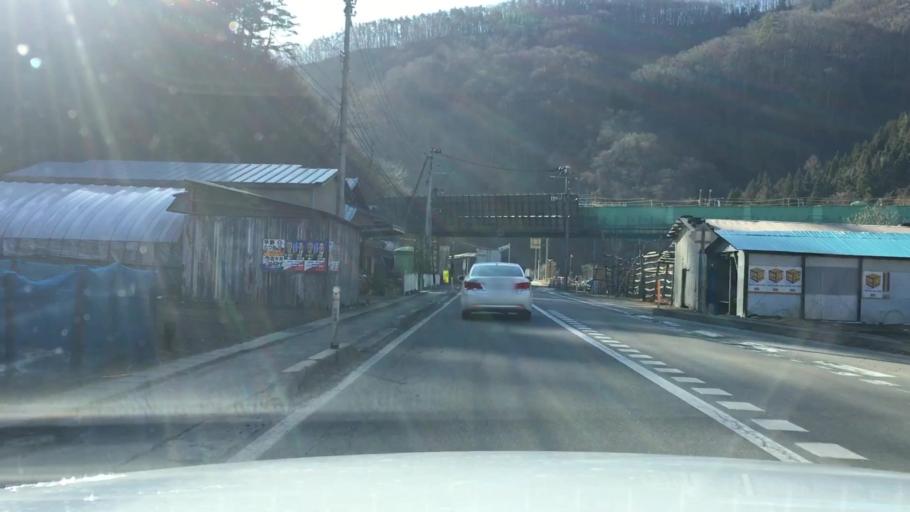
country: JP
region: Iwate
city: Miyako
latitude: 39.6007
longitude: 141.6474
